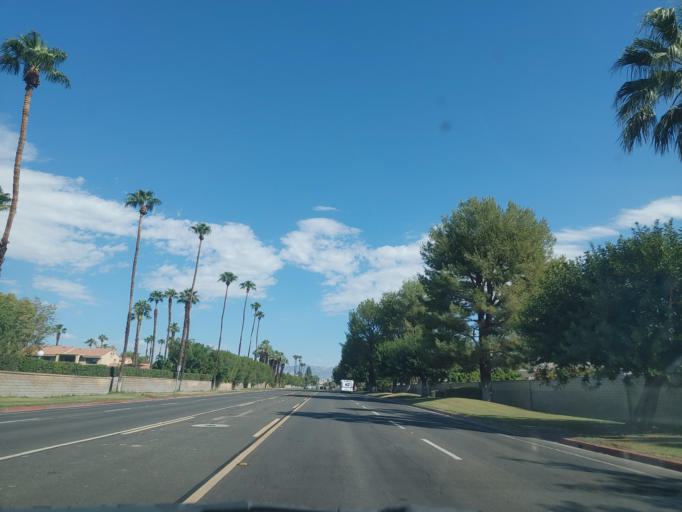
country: US
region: California
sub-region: Riverside County
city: Cathedral City
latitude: 33.7976
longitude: -116.4667
